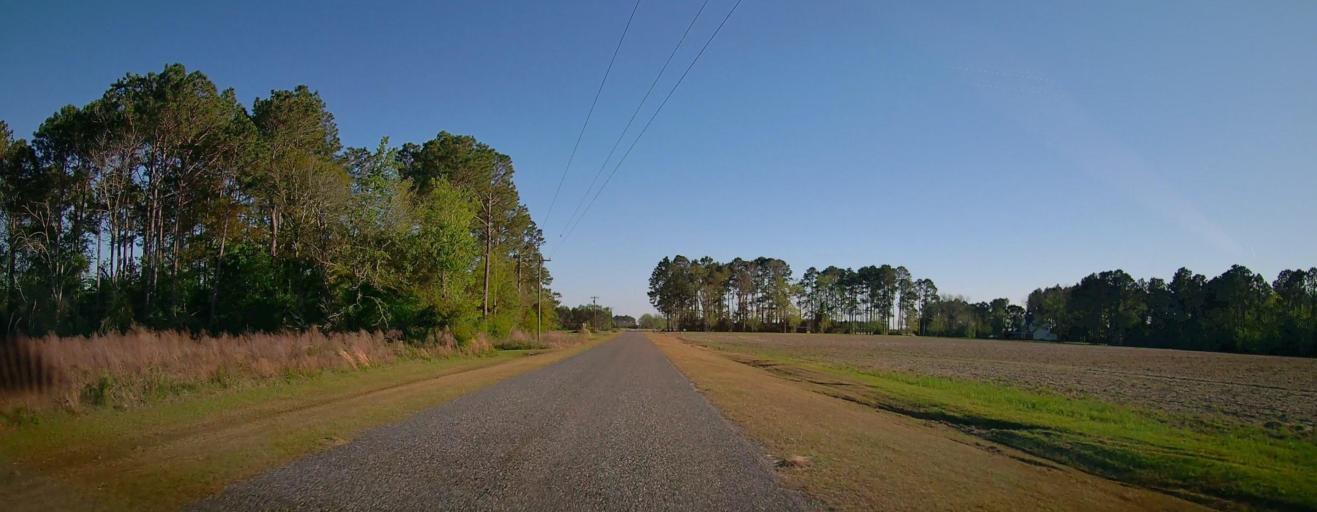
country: US
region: Georgia
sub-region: Ben Hill County
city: Fitzgerald
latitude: 31.6715
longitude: -83.1467
